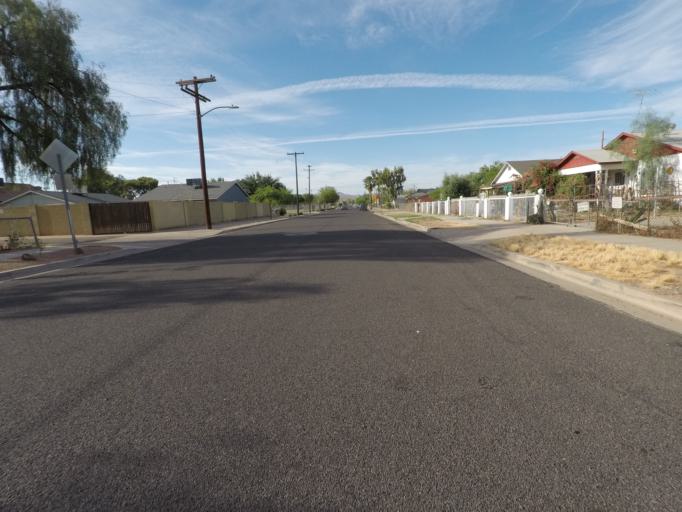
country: US
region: Arizona
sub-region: Maricopa County
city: Phoenix
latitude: 33.4397
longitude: -112.0725
